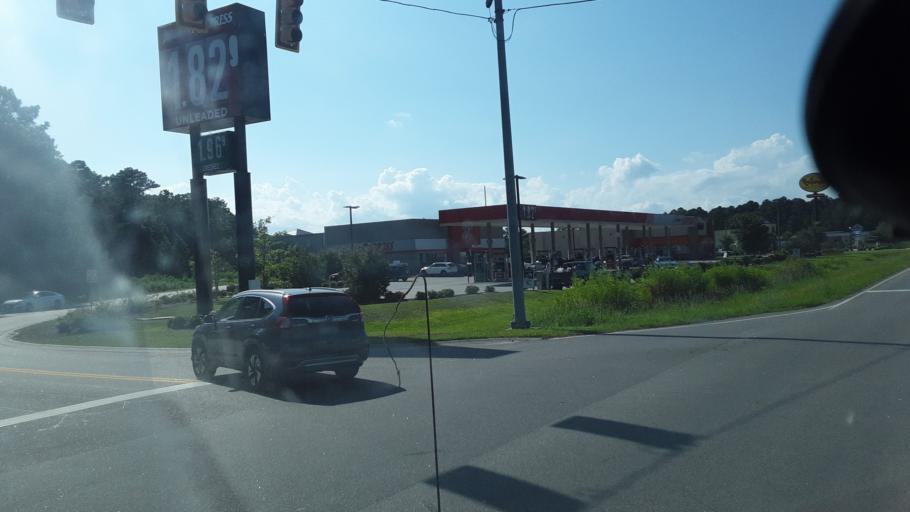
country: US
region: South Carolina
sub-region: Horry County
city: Myrtle Beach
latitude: 33.7585
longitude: -78.8572
